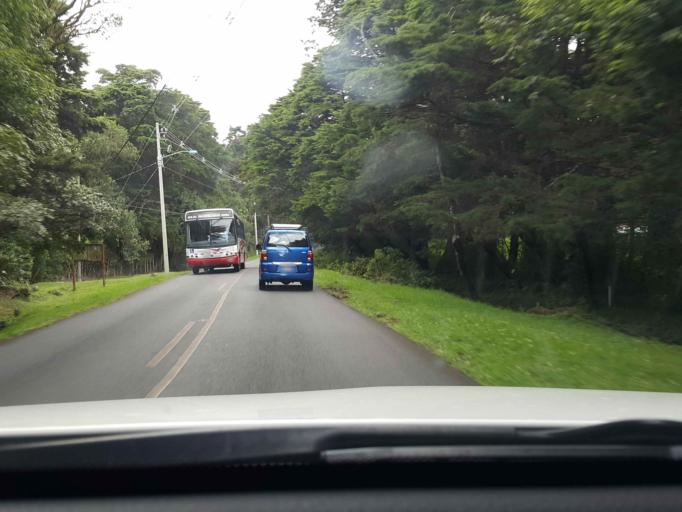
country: CR
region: Heredia
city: San Josecito
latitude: 10.0583
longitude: -84.0856
